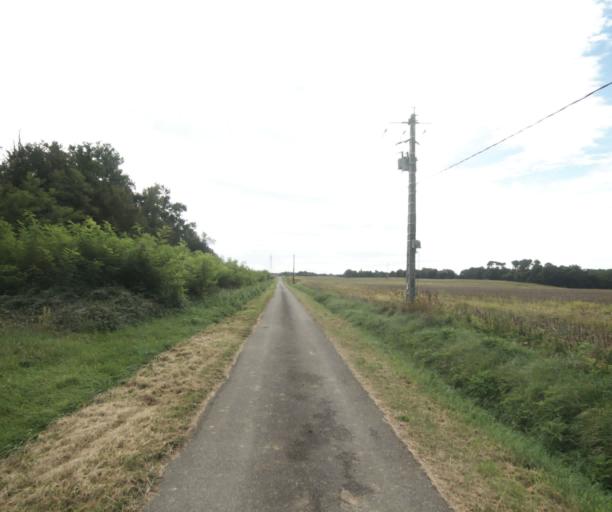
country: FR
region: Aquitaine
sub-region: Departement des Landes
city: Villeneuve-de-Marsan
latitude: 43.9065
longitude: -0.2246
